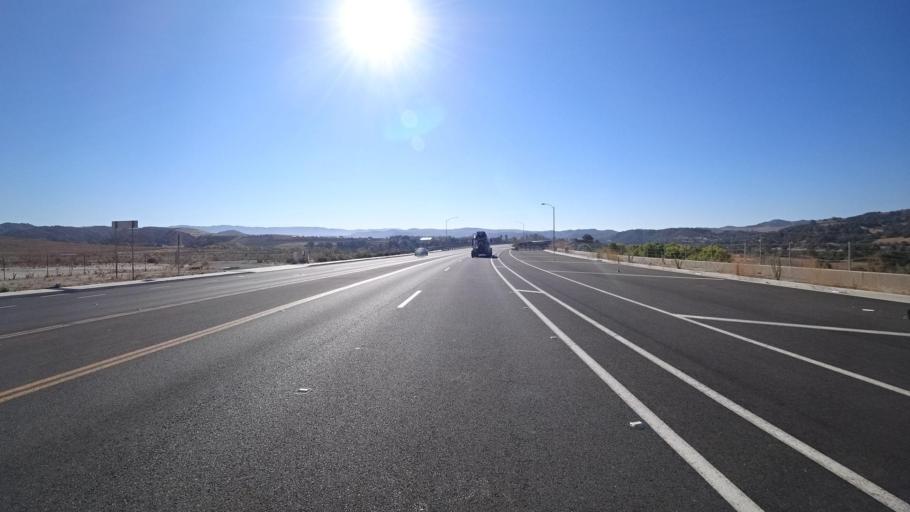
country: US
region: California
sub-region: Orange County
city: Ladera Ranch
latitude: 33.5264
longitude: -117.5971
